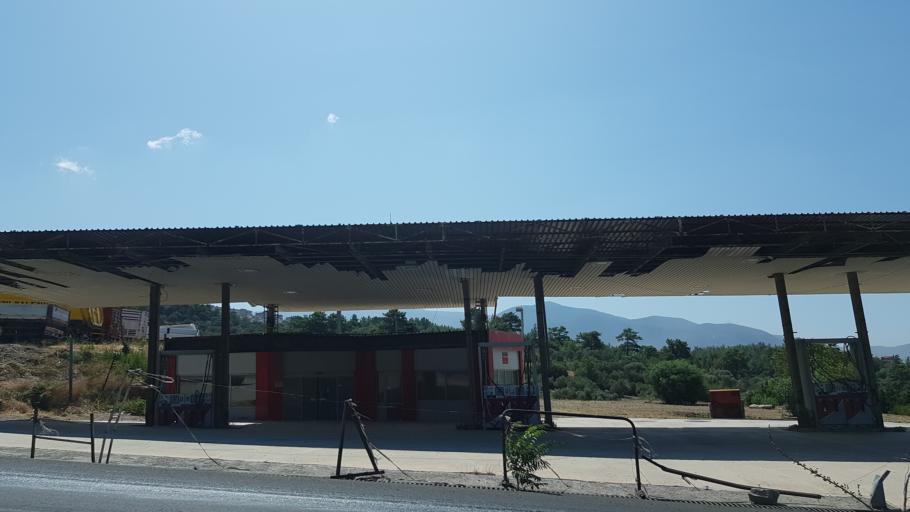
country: TR
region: Izmir
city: Bornova
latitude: 38.4780
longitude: 27.2351
